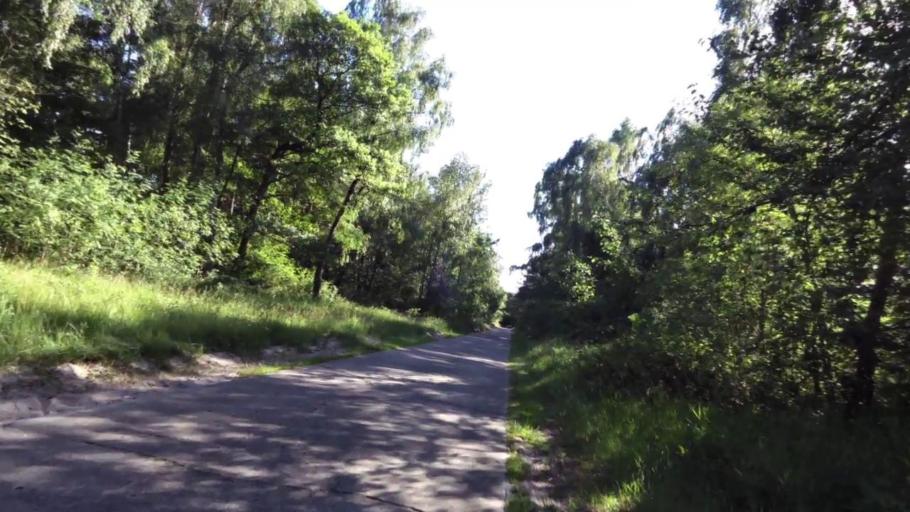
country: PL
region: West Pomeranian Voivodeship
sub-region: Powiat slawienski
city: Darlowo
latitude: 54.3652
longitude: 16.2889
